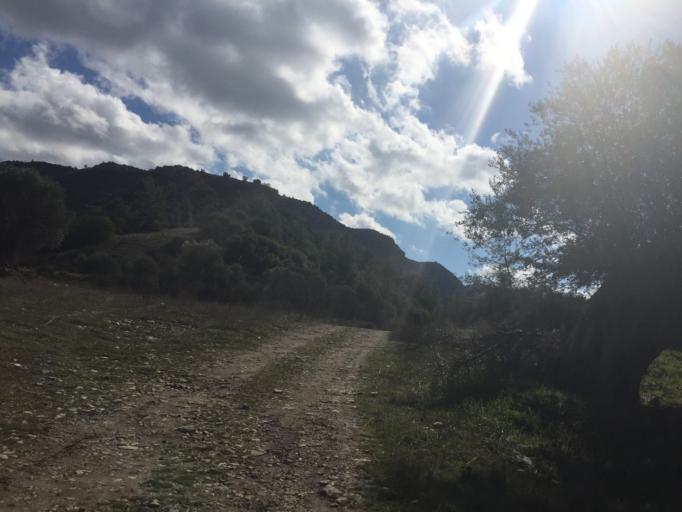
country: CY
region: Limassol
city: Pachna
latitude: 34.8857
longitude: 32.6773
